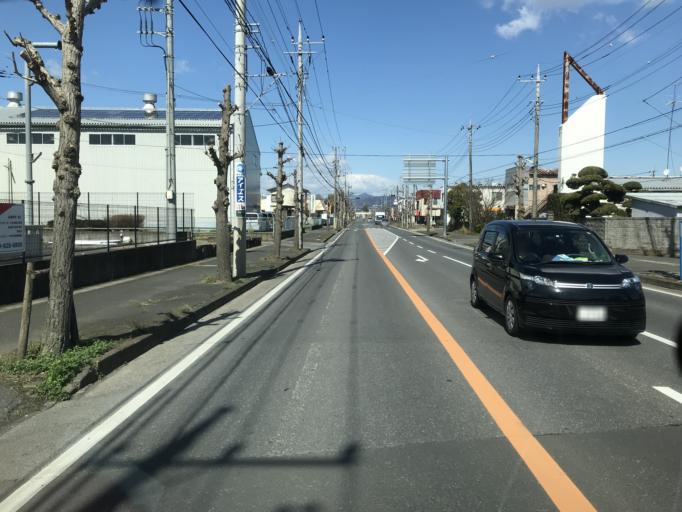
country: JP
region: Ibaraki
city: Ishioka
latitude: 36.1103
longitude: 140.2517
